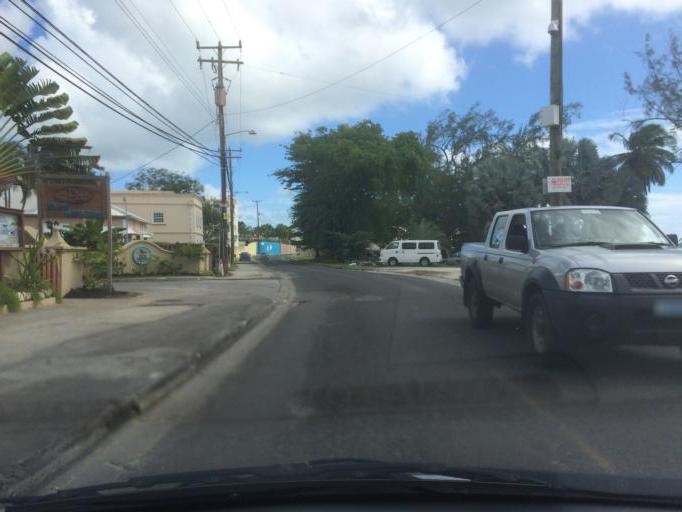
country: BB
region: Saint Michael
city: Bridgetown
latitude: 13.0740
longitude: -59.5882
